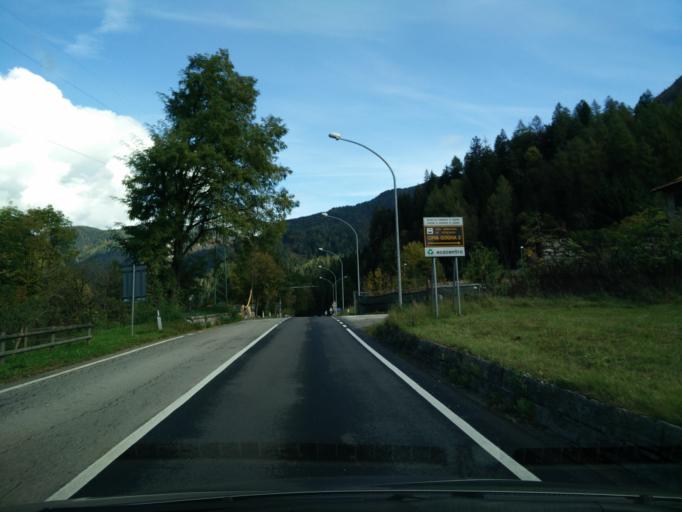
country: IT
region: Veneto
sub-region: Provincia di Belluno
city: Vigo di Cadore
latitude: 46.5171
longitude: 12.4648
